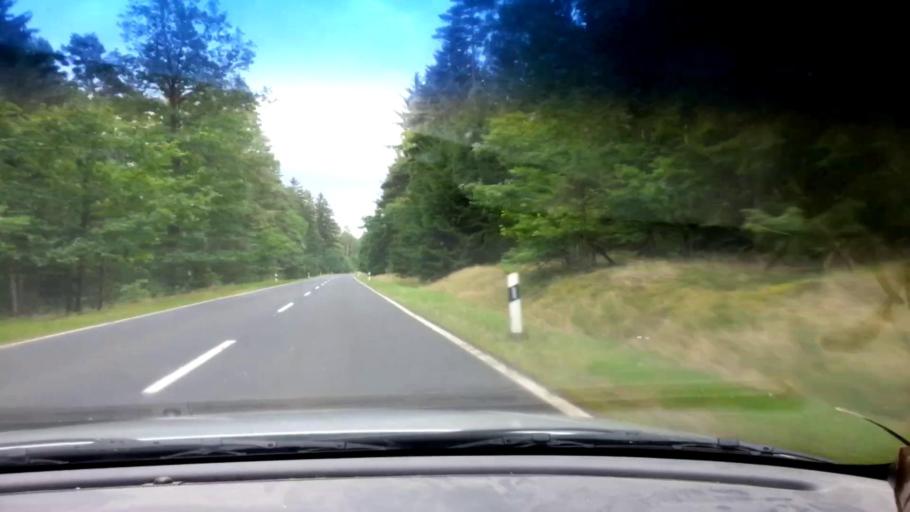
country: DE
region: Bavaria
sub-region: Upper Palatinate
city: Waldsassen
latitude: 50.0224
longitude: 12.3100
